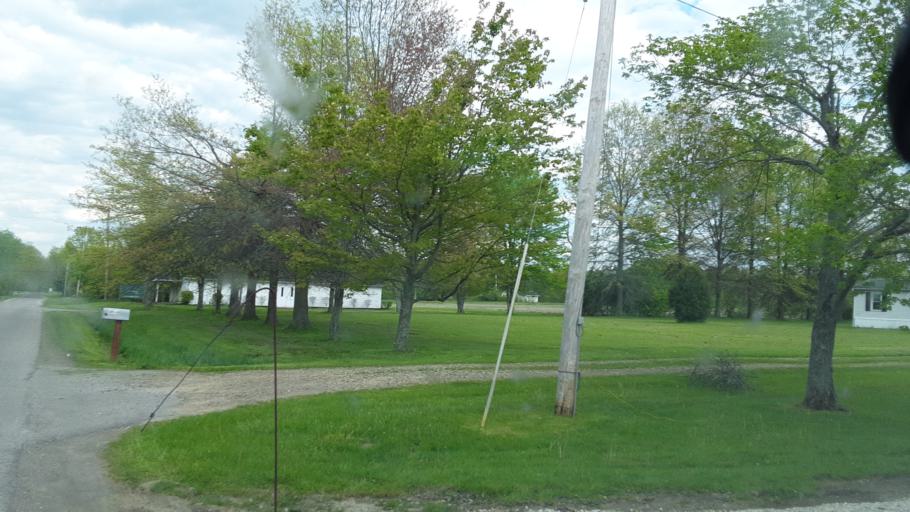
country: US
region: Ohio
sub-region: Portage County
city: Garrettsville
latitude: 41.3479
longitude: -81.0054
